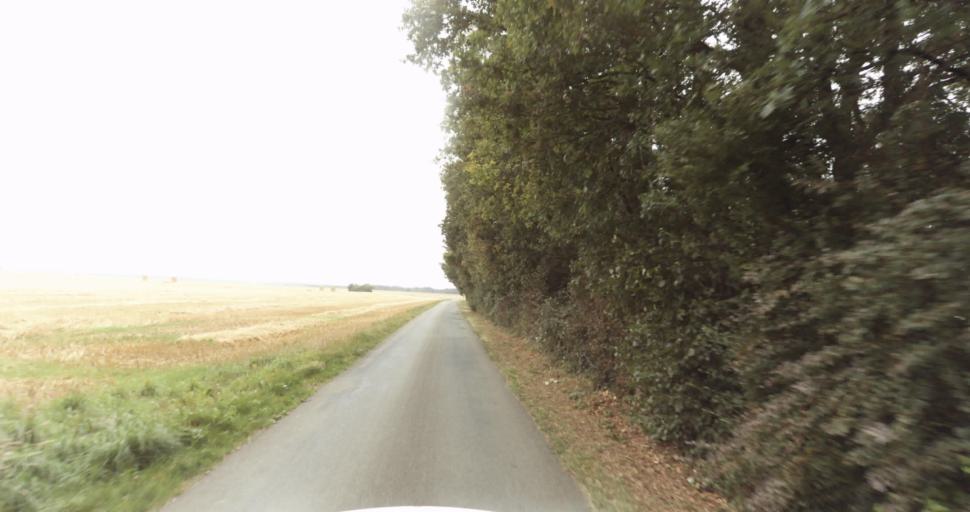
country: FR
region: Centre
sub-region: Departement d'Eure-et-Loir
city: Vert-en-Drouais
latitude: 48.7744
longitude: 1.2990
